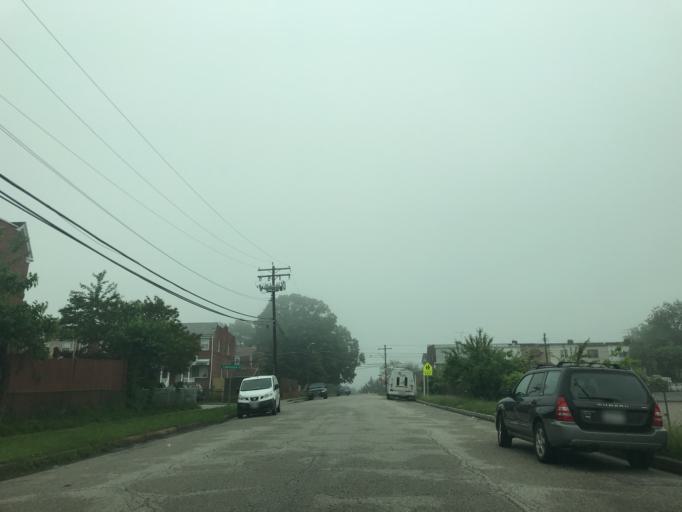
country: US
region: Maryland
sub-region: Baltimore County
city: Rosedale
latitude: 39.2960
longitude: -76.5200
